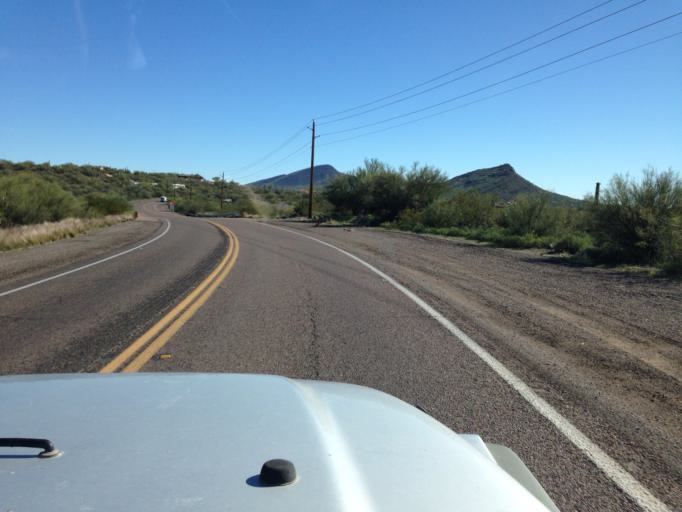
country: US
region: Arizona
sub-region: Maricopa County
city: New River
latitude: 33.9022
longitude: -112.0815
